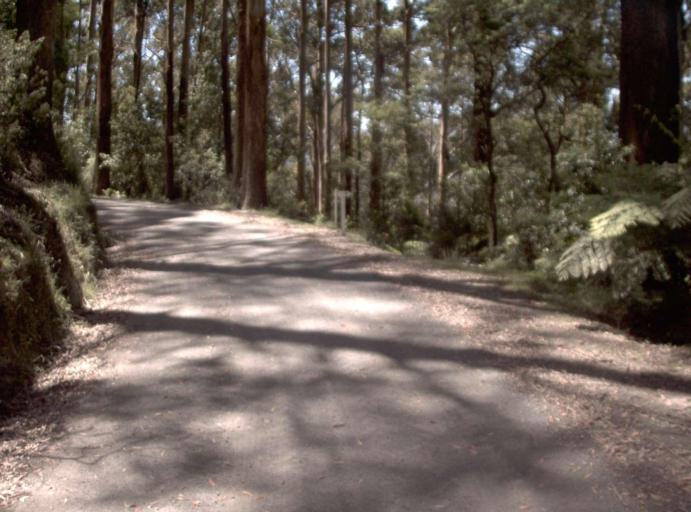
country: AU
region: Victoria
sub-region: Yarra Ranges
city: Millgrove
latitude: -37.7086
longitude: 145.7240
